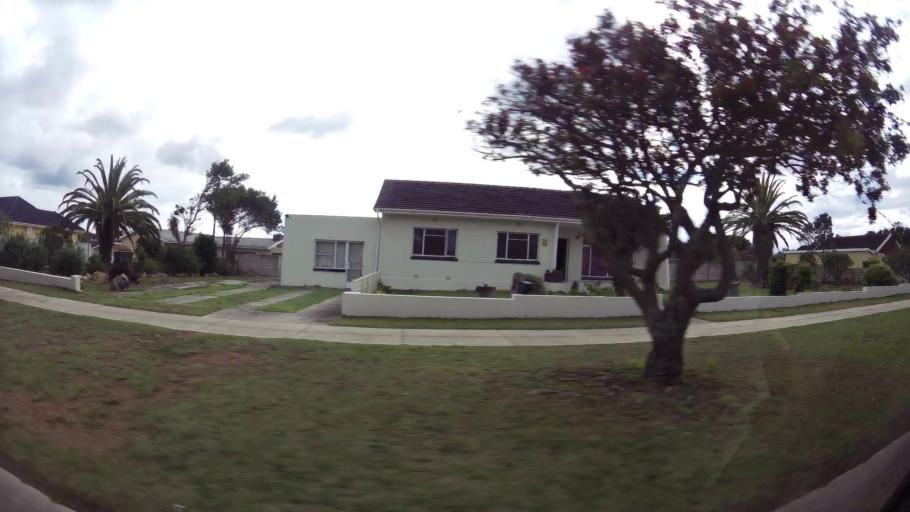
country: ZA
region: Eastern Cape
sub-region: Nelson Mandela Bay Metropolitan Municipality
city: Port Elizabeth
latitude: -33.9395
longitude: 25.5212
